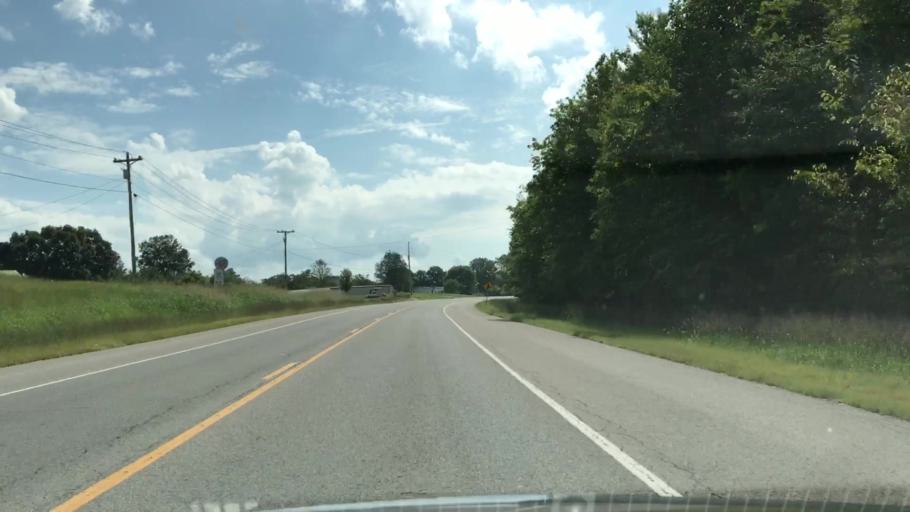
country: US
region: Tennessee
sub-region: Sumner County
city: Westmoreland
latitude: 36.5443
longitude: -86.2122
